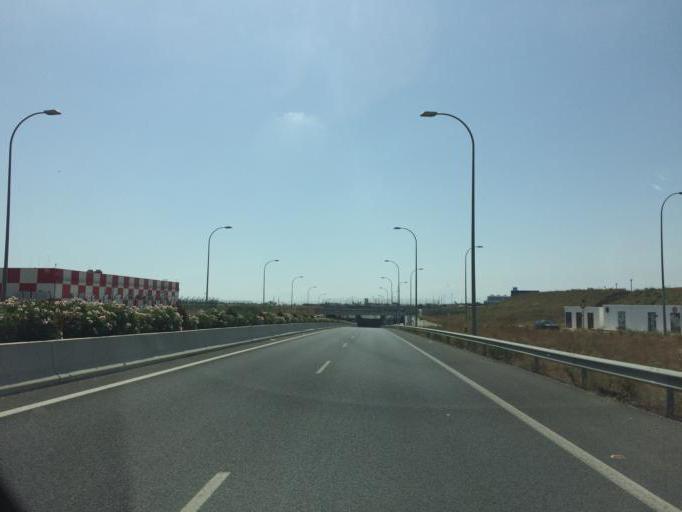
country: ES
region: Andalusia
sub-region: Provincia de Malaga
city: Alhaurin de la Torre
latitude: 36.6878
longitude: -4.5076
